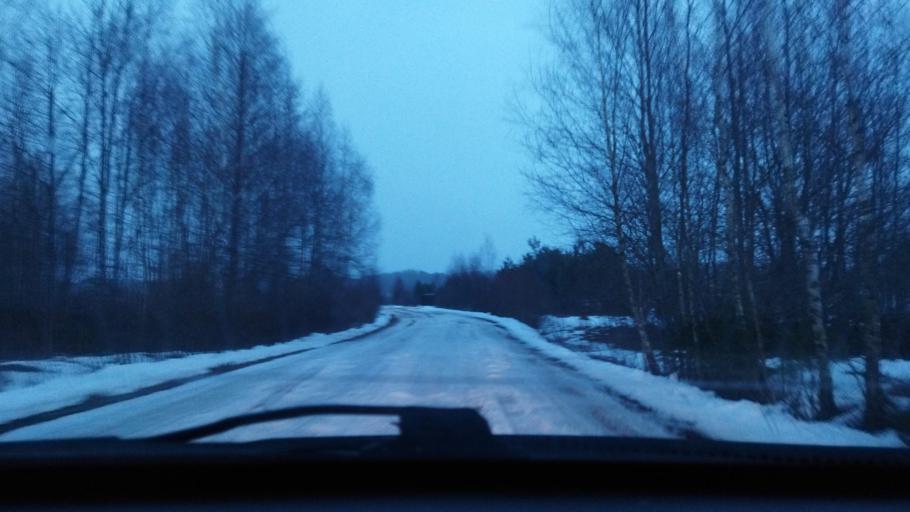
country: BY
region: Minsk
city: Svir
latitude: 54.9376
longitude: 26.3946
